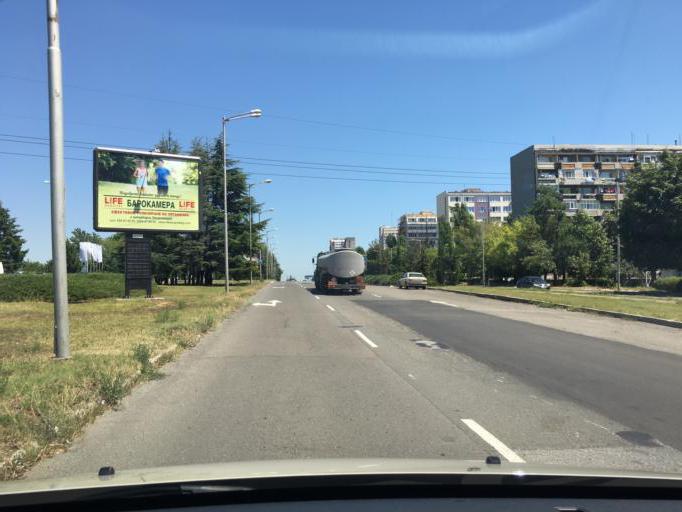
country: BG
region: Burgas
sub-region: Obshtina Burgas
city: Burgas
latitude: 42.5233
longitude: 27.4450
